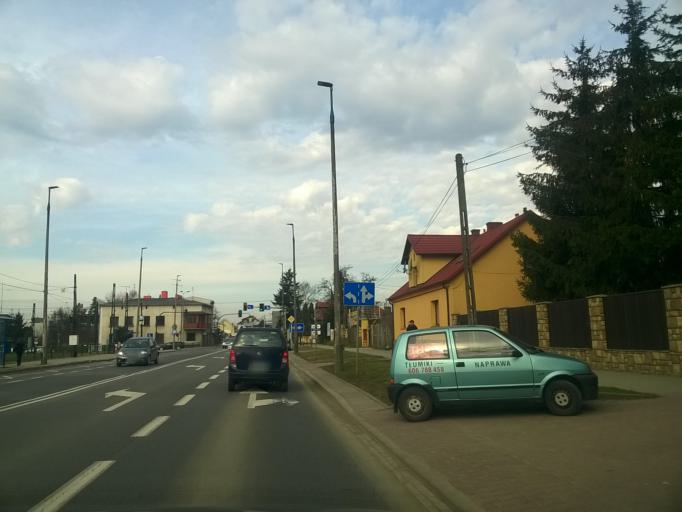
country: PL
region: Lesser Poland Voivodeship
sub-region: Powiat krakowski
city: Rzaska
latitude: 50.0823
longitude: 19.8821
